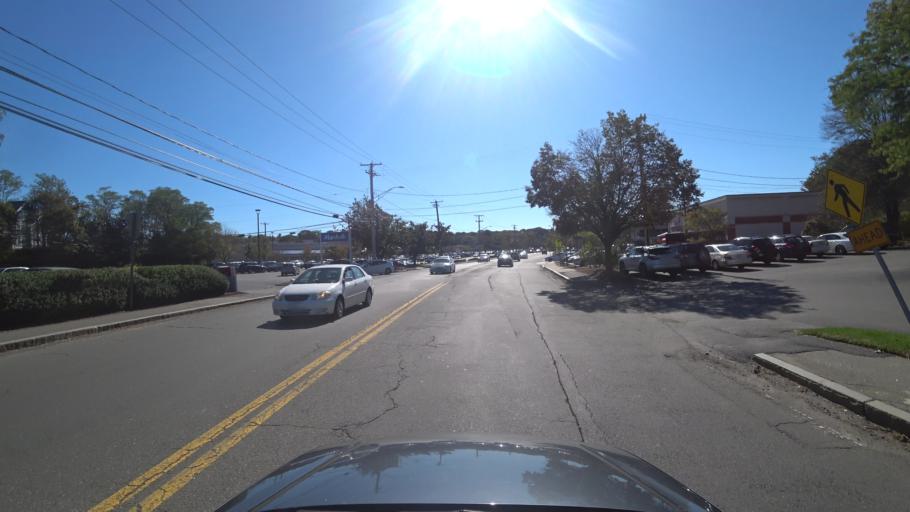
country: US
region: Massachusetts
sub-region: Essex County
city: Swampscott
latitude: 42.4836
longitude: -70.9005
